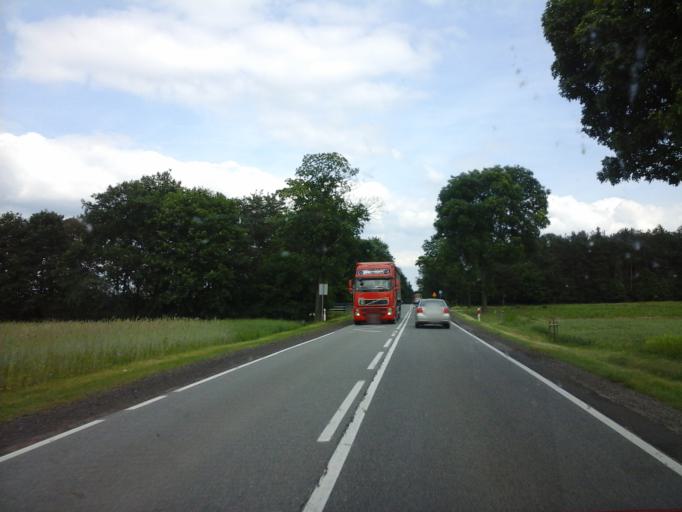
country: PL
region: Lodz Voivodeship
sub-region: Powiat opoczynski
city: Paradyz
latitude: 51.3122
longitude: 20.0820
